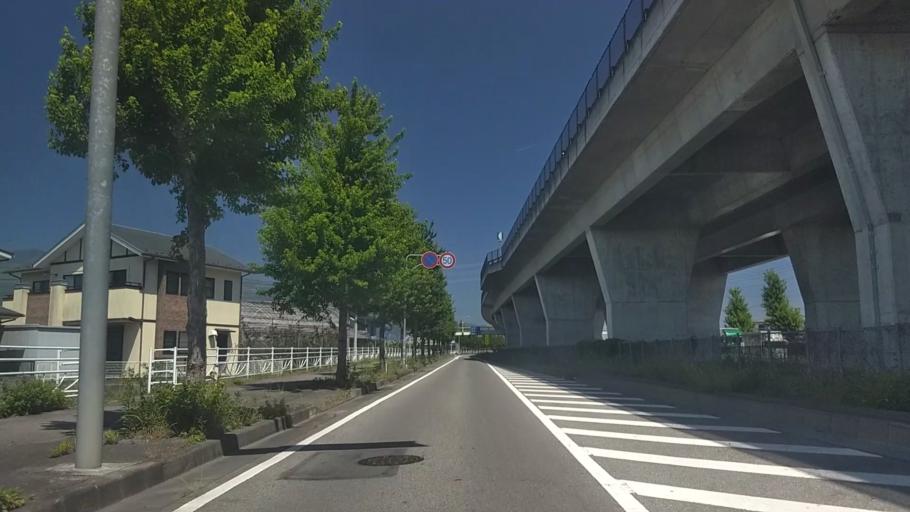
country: JP
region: Yamanashi
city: Ryuo
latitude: 35.6203
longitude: 138.4778
